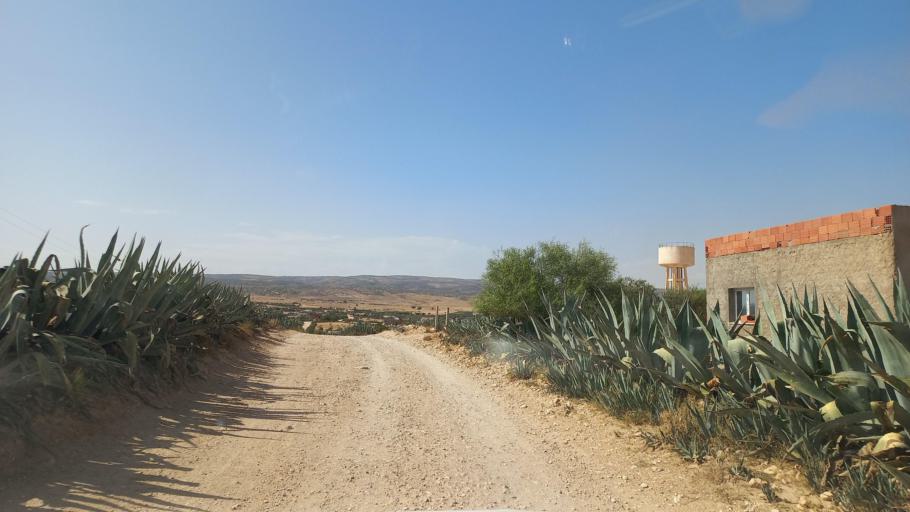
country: TN
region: Al Qasrayn
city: Kasserine
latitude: 35.2722
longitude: 8.9494
